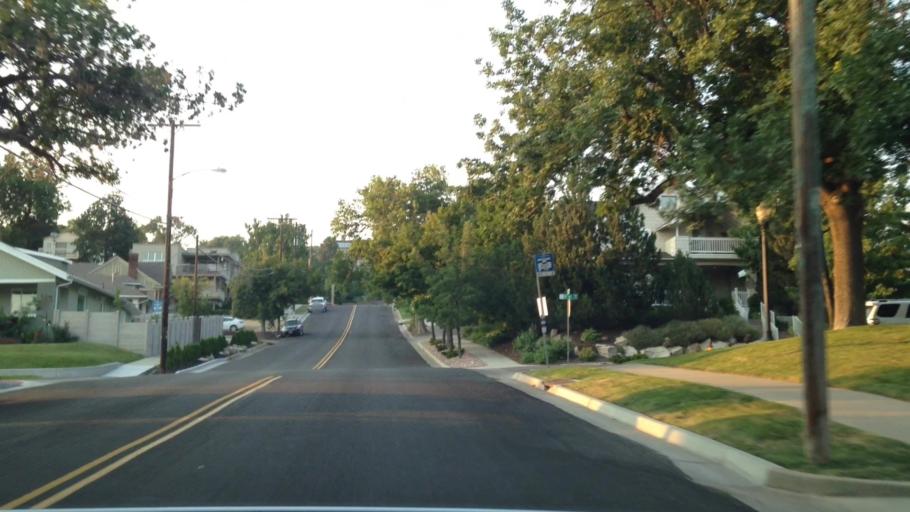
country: US
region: Utah
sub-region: Salt Lake County
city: Salt Lake City
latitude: 40.7805
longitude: -111.8774
